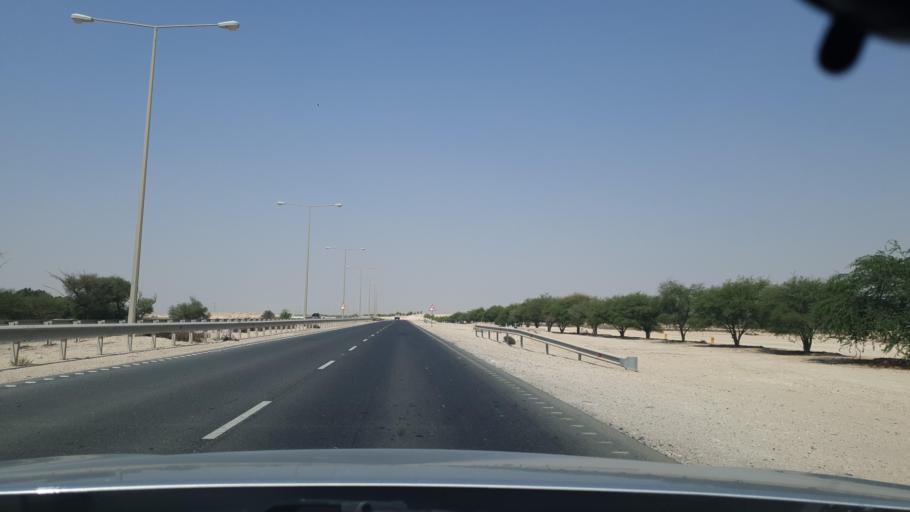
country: QA
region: Al Khawr
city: Al Khawr
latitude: 25.7307
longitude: 51.4947
